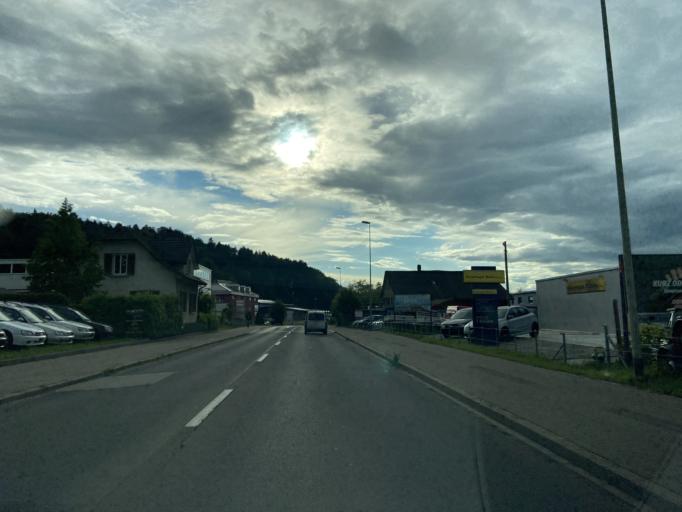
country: CH
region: Zurich
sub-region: Bezirk Winterthur
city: Elsau-Raeterschen / Raeterschen
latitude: 47.4994
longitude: 8.7904
